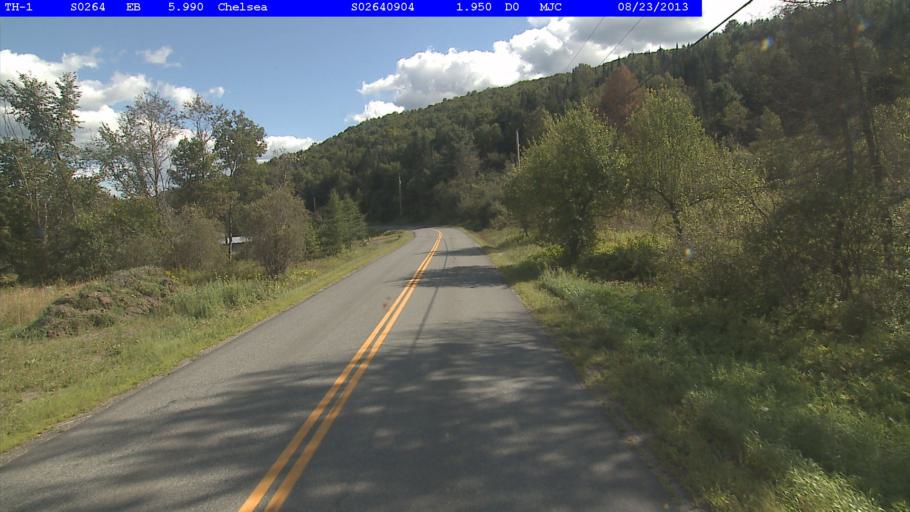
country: US
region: Vermont
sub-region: Orange County
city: Chelsea
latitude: 43.9686
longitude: -72.4780
